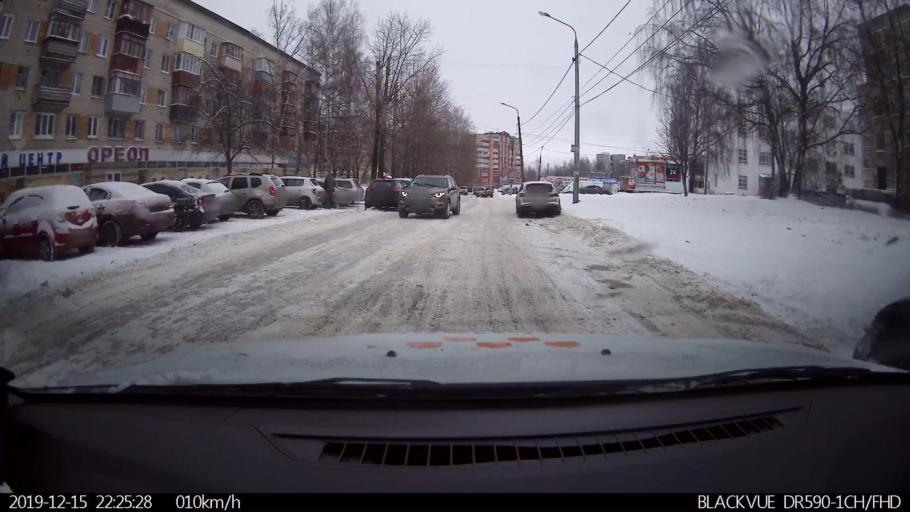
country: RU
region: Nizjnij Novgorod
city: Nizhniy Novgorod
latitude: 56.2385
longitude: 43.9619
